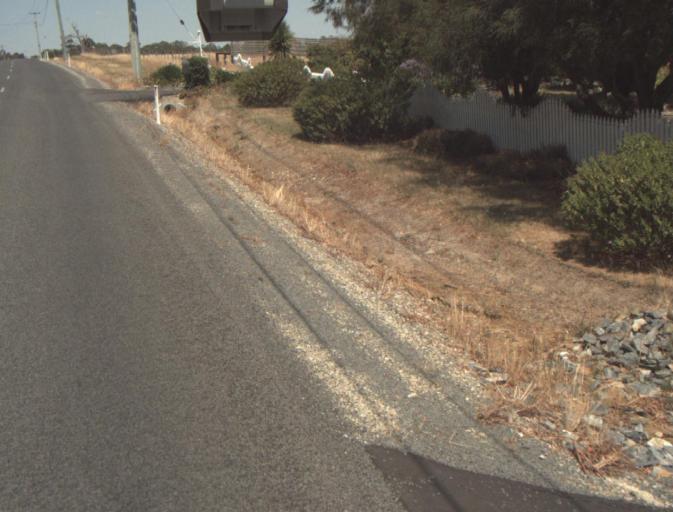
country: AU
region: Tasmania
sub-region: Launceston
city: Newstead
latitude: -41.4805
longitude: 147.1906
